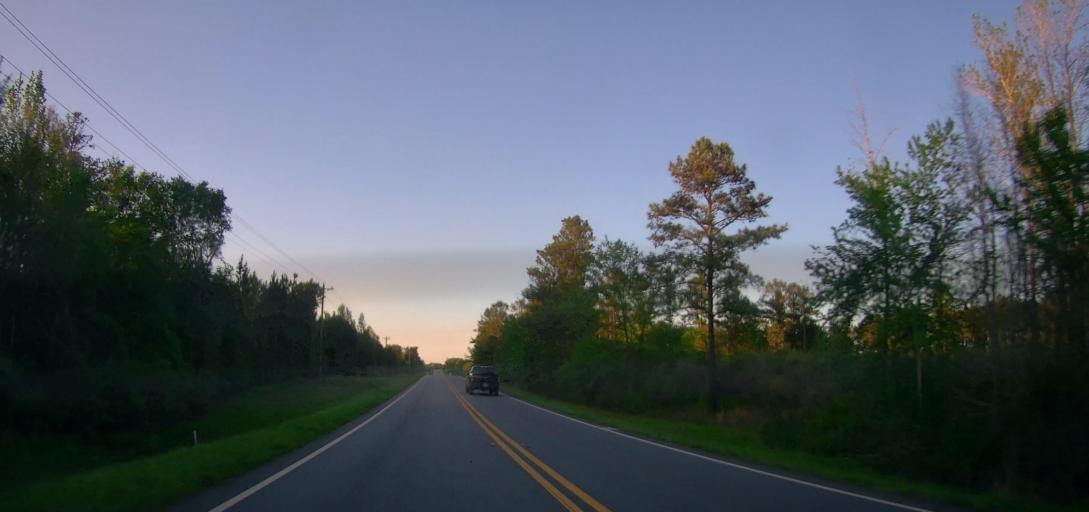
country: US
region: Georgia
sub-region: Talbot County
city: Talbotton
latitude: 32.5637
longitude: -84.5680
